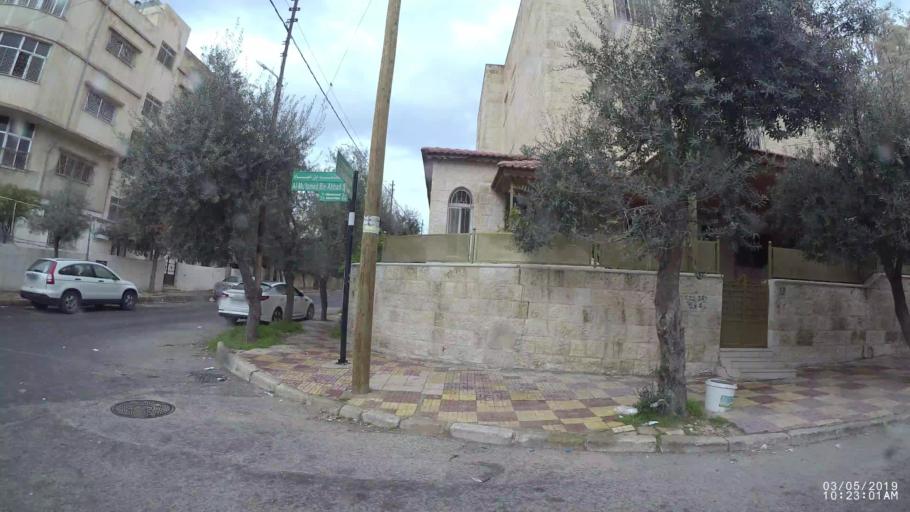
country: JO
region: Amman
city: Amman
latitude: 31.9822
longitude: 35.9274
